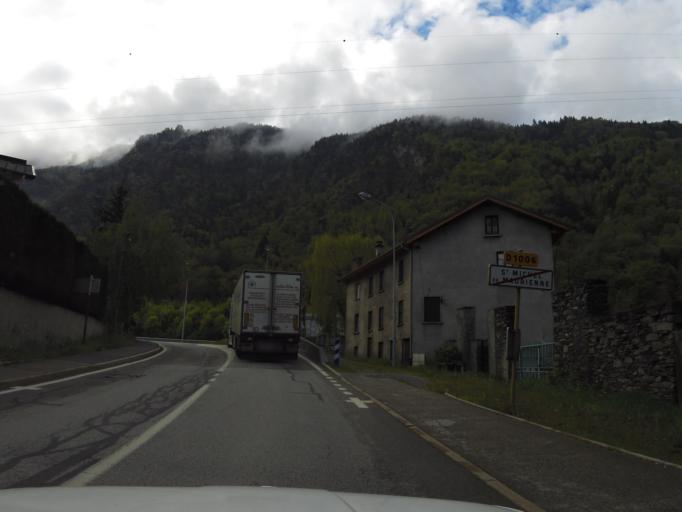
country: FR
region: Rhone-Alpes
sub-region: Departement de la Savoie
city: Saint-Michel-de-Maurienne
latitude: 45.2107
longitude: 6.4791
